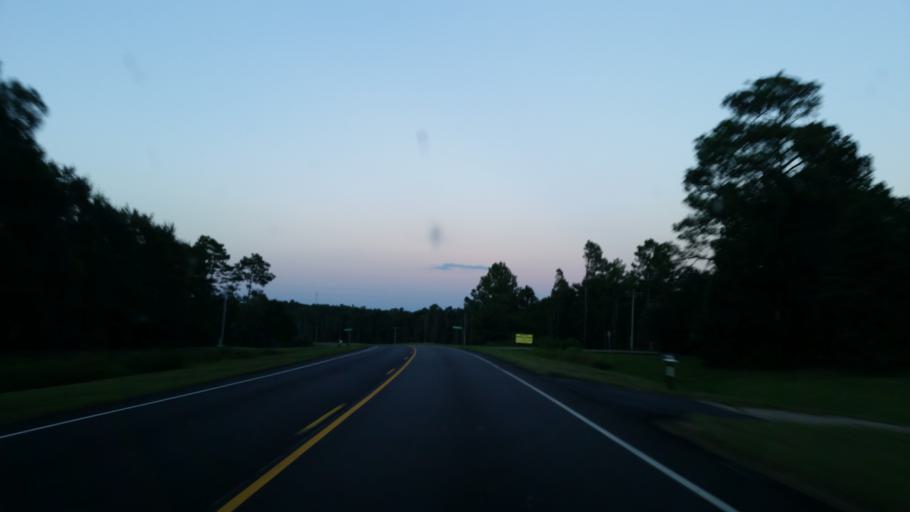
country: US
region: Alabama
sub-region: Baldwin County
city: Robertsdale
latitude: 30.5639
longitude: -87.6770
